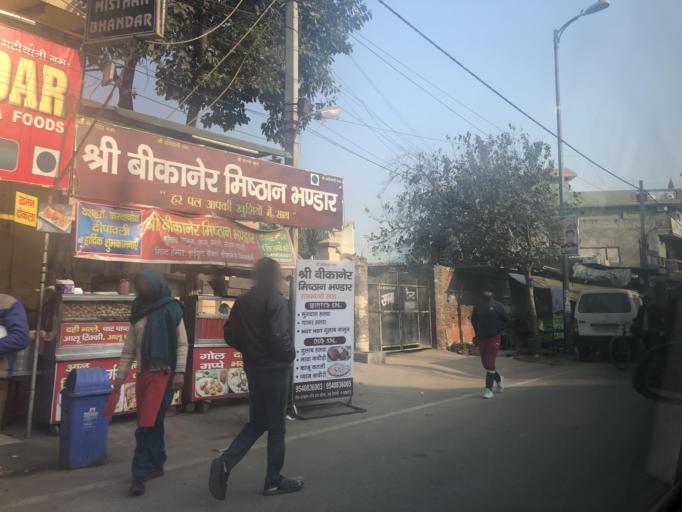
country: IN
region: Haryana
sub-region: Gurgaon
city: Gurgaon
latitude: 28.5608
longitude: 77.0024
